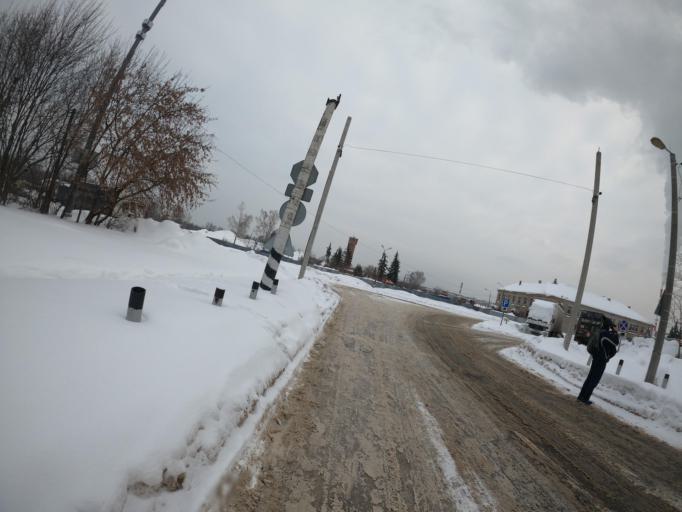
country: RU
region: Moskovskaya
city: Elektrogorsk
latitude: 55.8658
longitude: 38.7845
